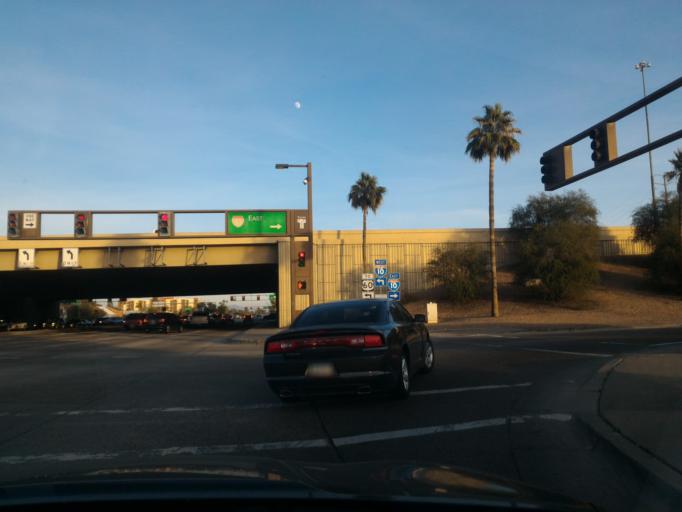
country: US
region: Arizona
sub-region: Maricopa County
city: Guadalupe
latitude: 33.3781
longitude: -111.9689
